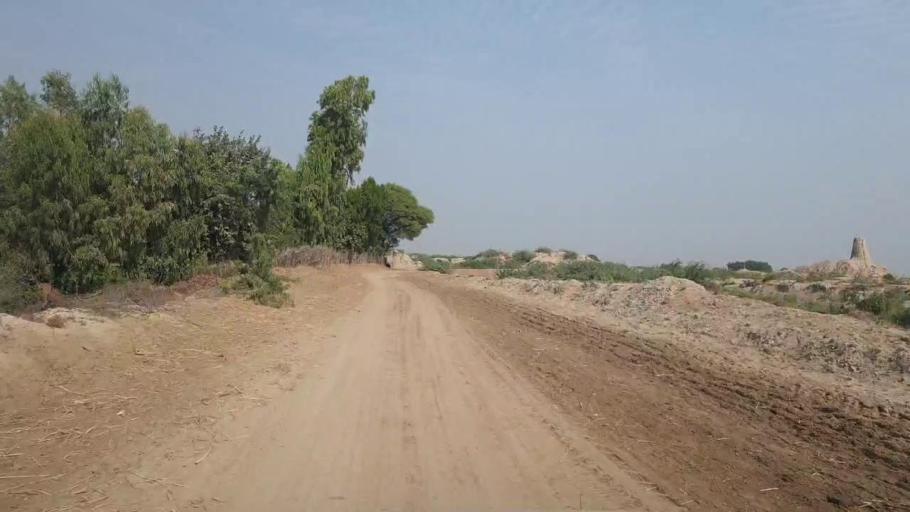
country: PK
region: Sindh
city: Tando Muhammad Khan
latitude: 25.1594
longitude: 68.4690
